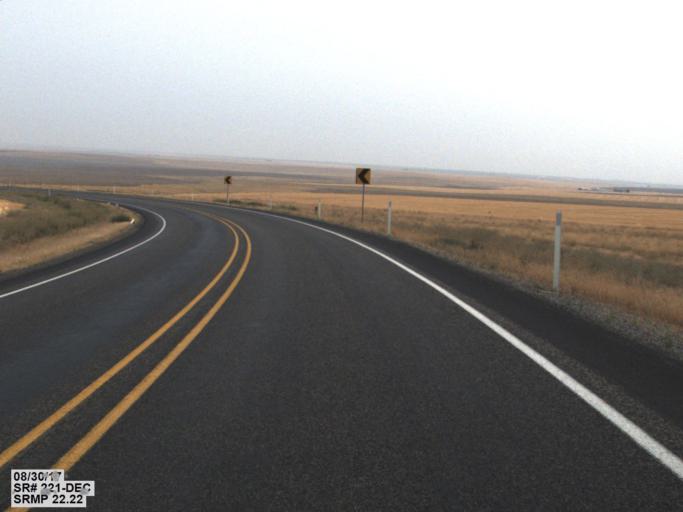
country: US
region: Washington
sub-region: Benton County
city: Prosser
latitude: 46.1880
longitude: -119.7039
